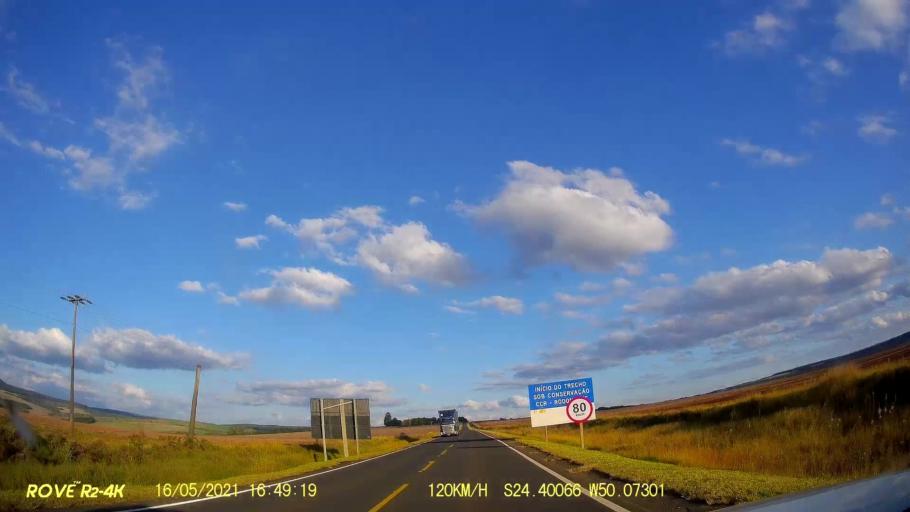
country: BR
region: Parana
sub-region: Pirai Do Sul
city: Pirai do Sul
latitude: -24.4008
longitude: -50.0729
